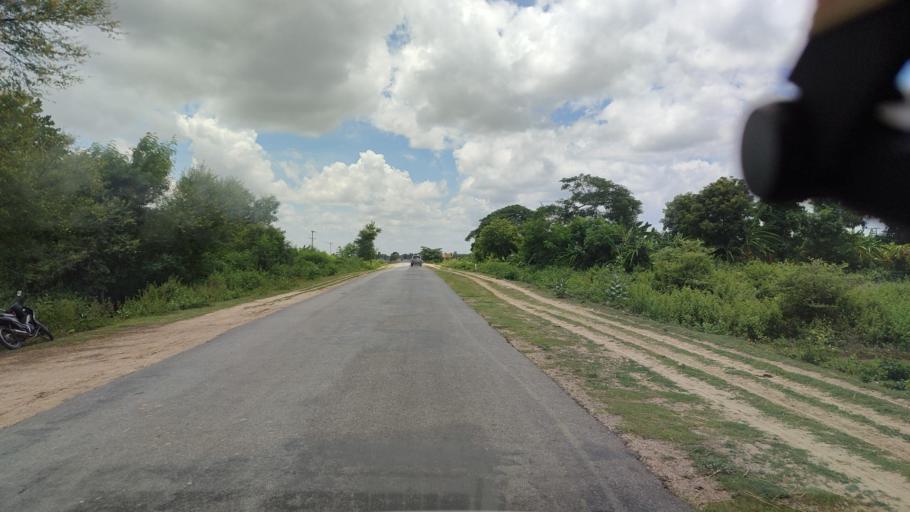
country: MM
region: Magway
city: Taungdwingyi
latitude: 20.1915
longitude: 95.4252
